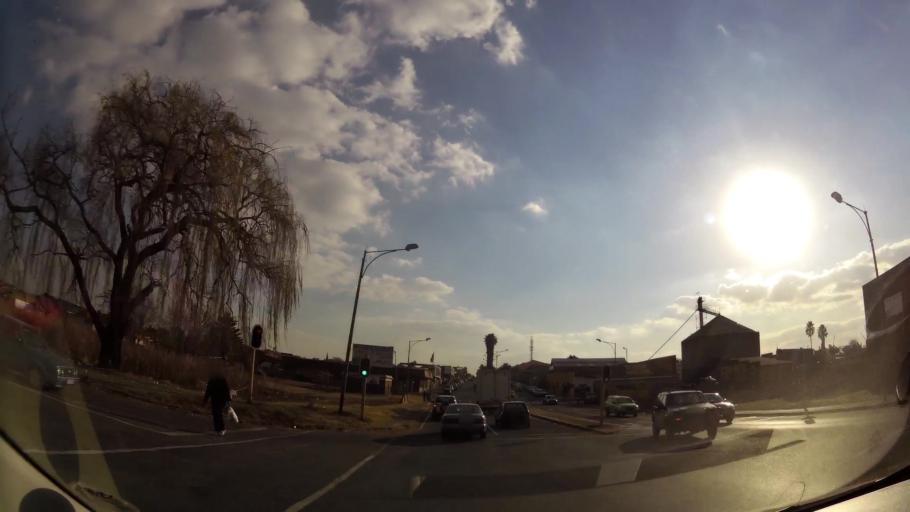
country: ZA
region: Gauteng
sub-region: West Rand District Municipality
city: Krugersdorp
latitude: -26.0981
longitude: 27.7537
